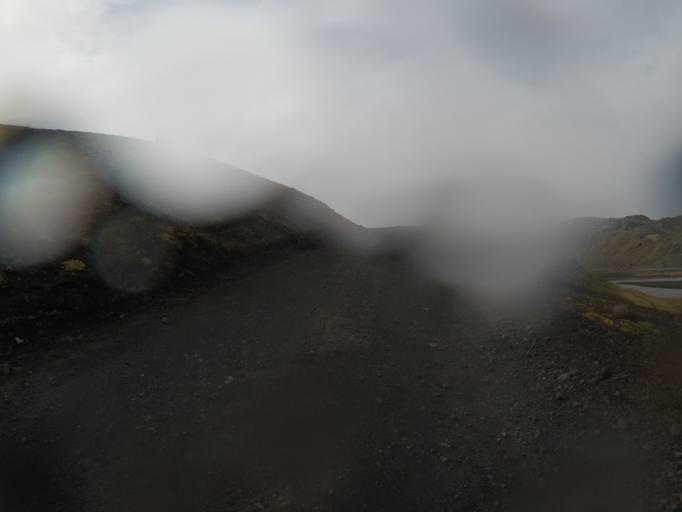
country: IS
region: South
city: Vestmannaeyjar
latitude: 63.9812
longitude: -18.8655
